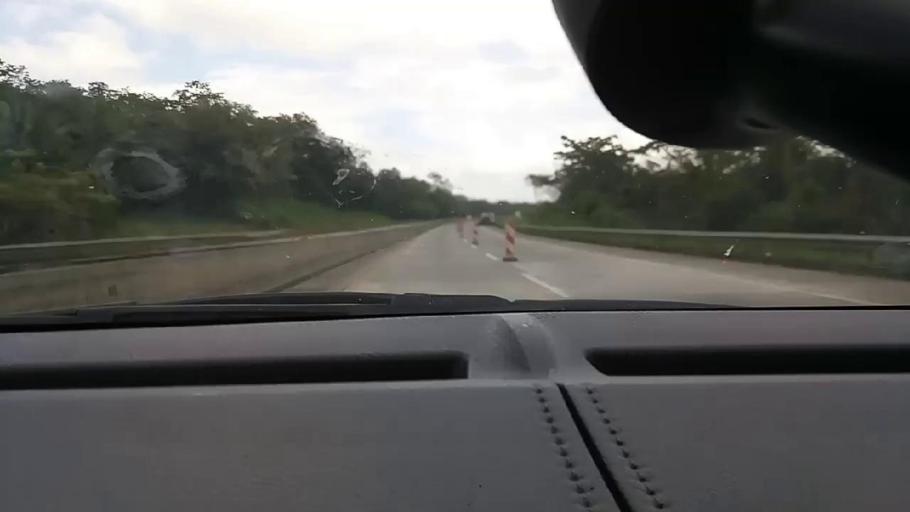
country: PA
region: Panama
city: Chilibre
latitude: 9.1656
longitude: -79.6392
